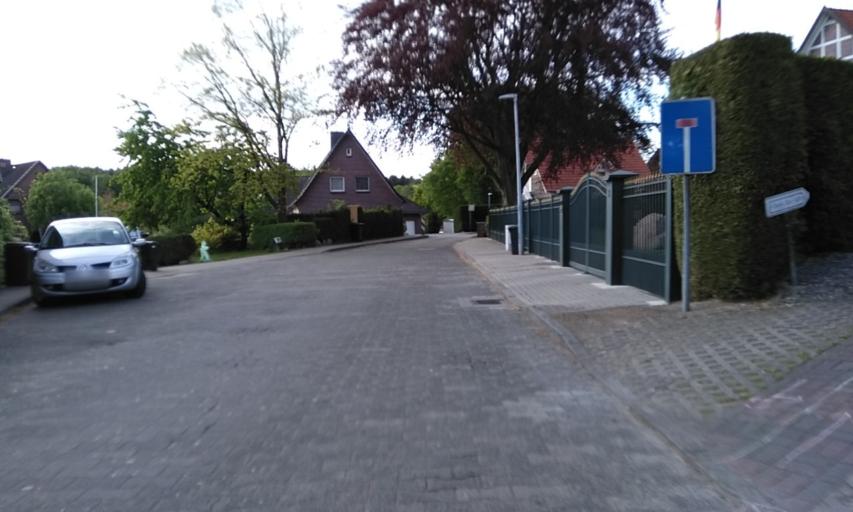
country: DE
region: Lower Saxony
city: Nottensdorf
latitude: 53.4804
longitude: 9.6171
